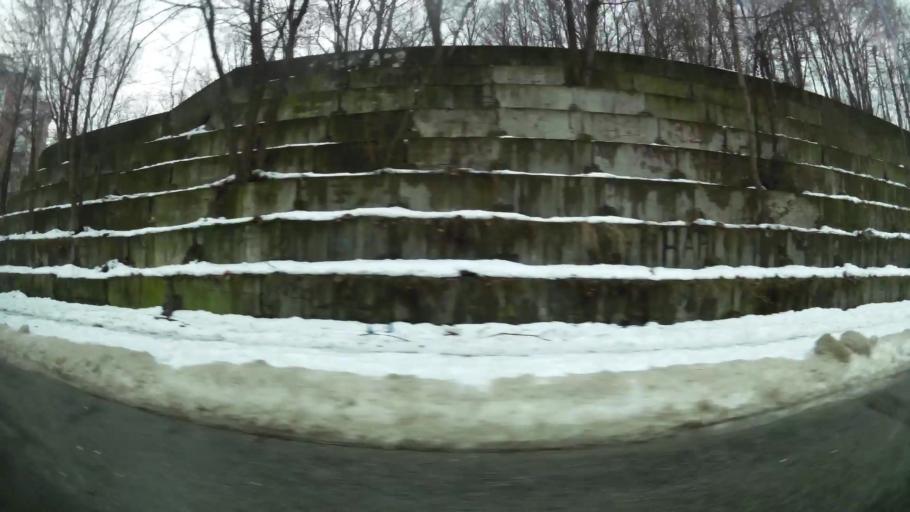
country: RS
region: Central Serbia
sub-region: Belgrade
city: Zvezdara
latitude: 44.7738
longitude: 20.5091
